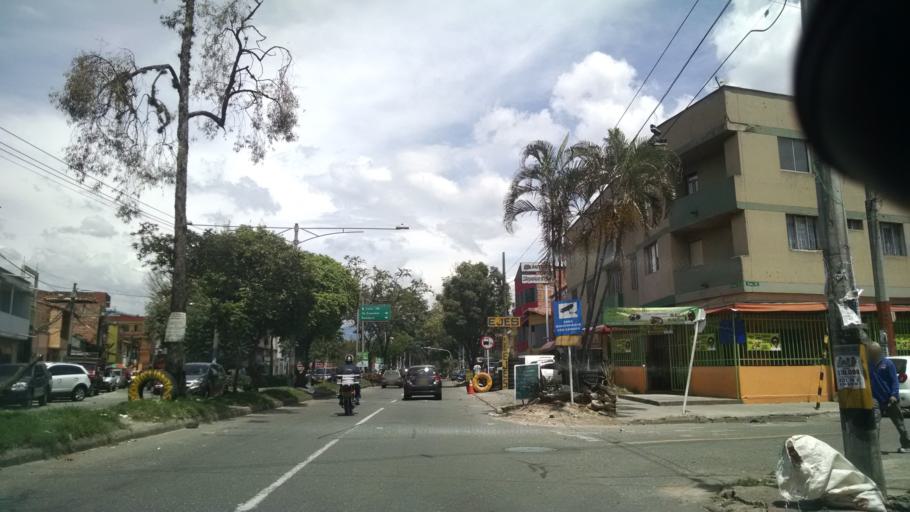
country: CO
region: Antioquia
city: Medellin
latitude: 6.2255
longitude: -75.5838
